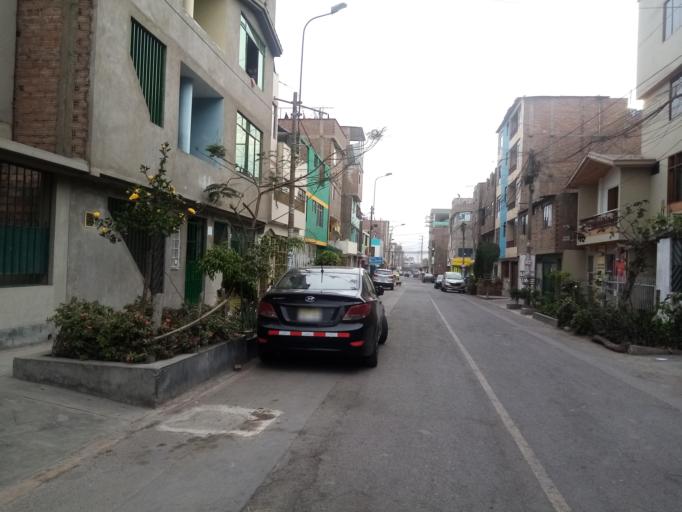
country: PE
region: Lima
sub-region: Lima
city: Vitarte
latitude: -12.0444
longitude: -76.9552
